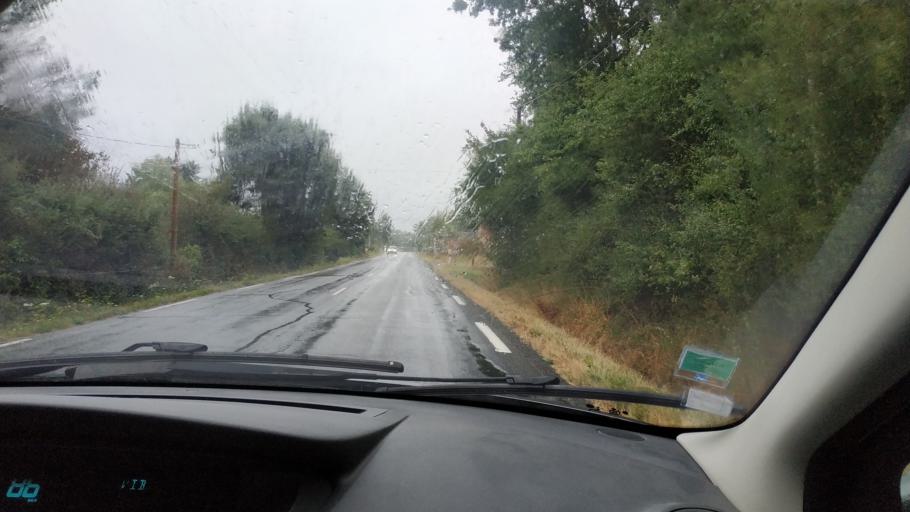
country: FR
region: Centre
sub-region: Departement du Loiret
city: Bellegarde
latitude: 47.9463
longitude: 2.3805
